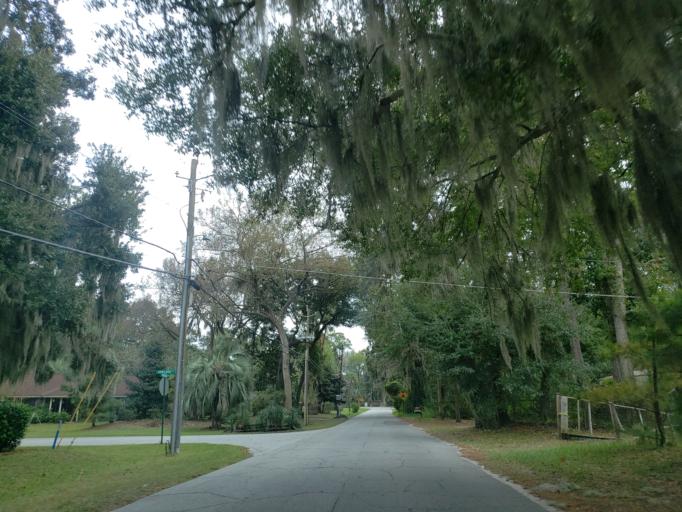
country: US
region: Georgia
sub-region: Chatham County
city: Montgomery
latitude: 31.9436
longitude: -81.1201
